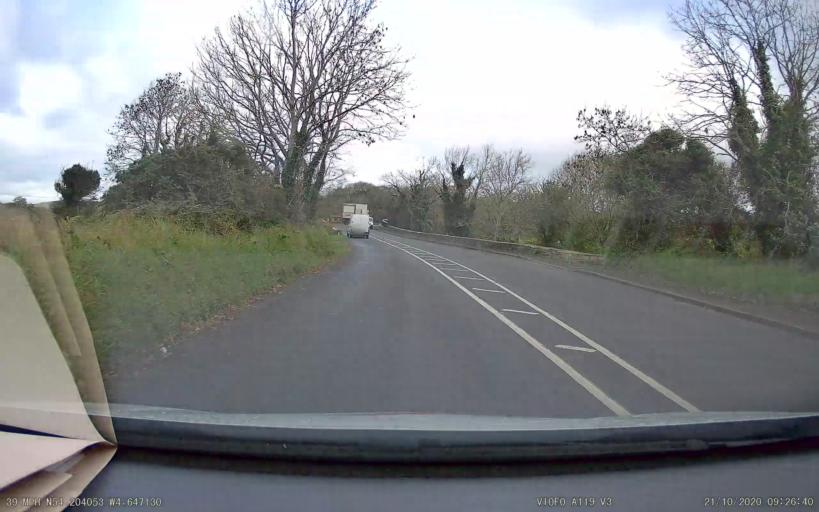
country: IM
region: Castletown
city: Castletown
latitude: 54.2040
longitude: -4.6479
